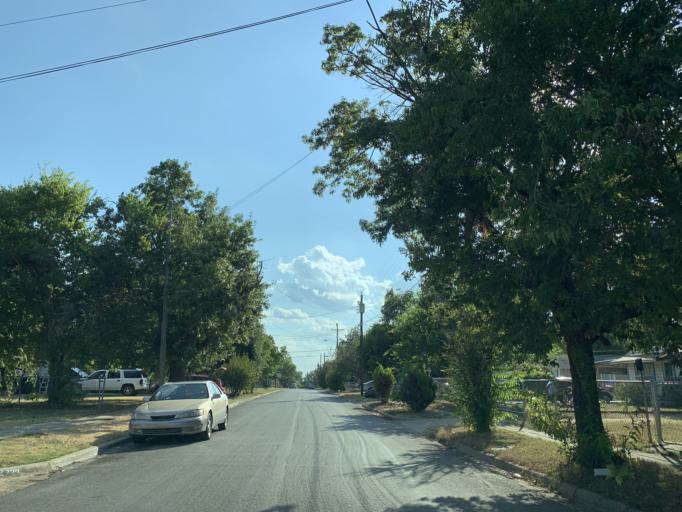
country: US
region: Texas
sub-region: Dallas County
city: Hutchins
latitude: 32.6973
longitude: -96.7790
